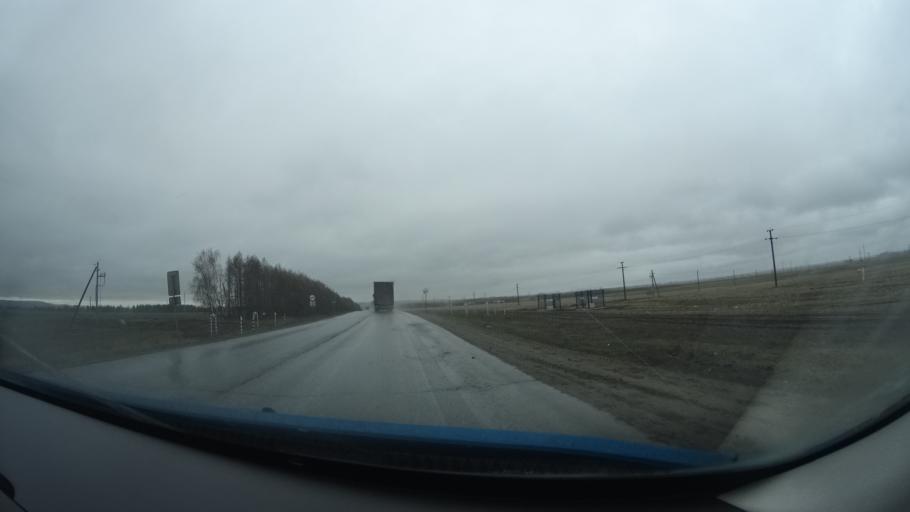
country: RU
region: Bashkortostan
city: Kandry
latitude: 54.5302
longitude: 54.0697
